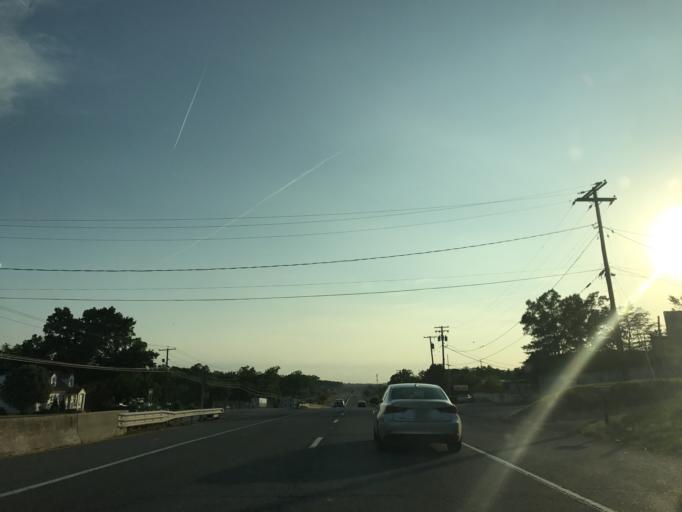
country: US
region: Maryland
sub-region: Harford County
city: Joppatowne
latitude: 39.4309
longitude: -76.3439
